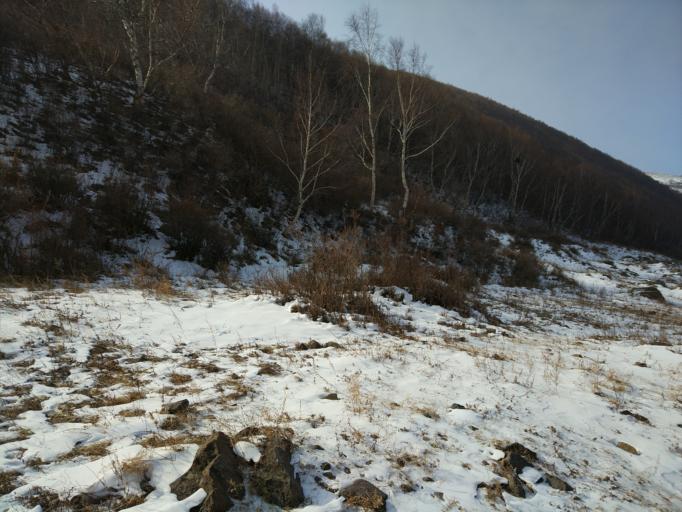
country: CN
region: Hebei
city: Xiwanzi
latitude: 40.8561
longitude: 115.4562
